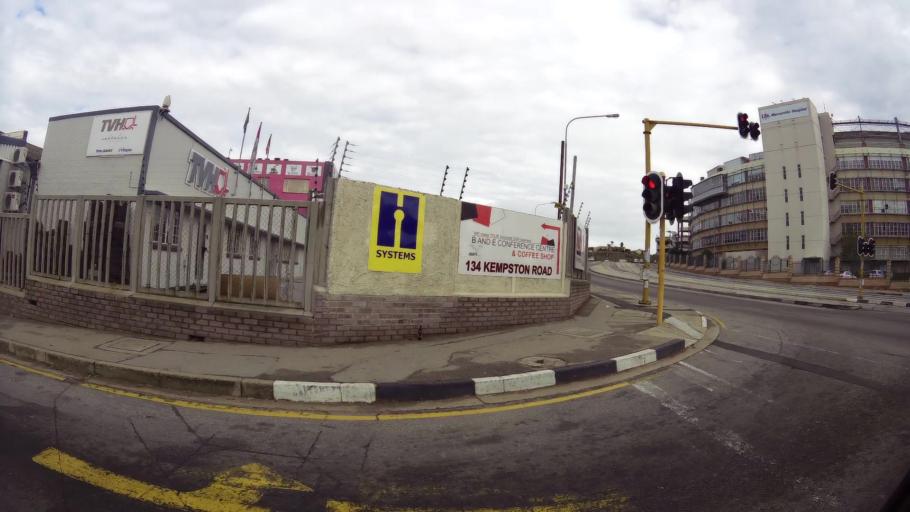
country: ZA
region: Eastern Cape
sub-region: Nelson Mandela Bay Metropolitan Municipality
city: Port Elizabeth
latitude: -33.9363
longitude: 25.5839
